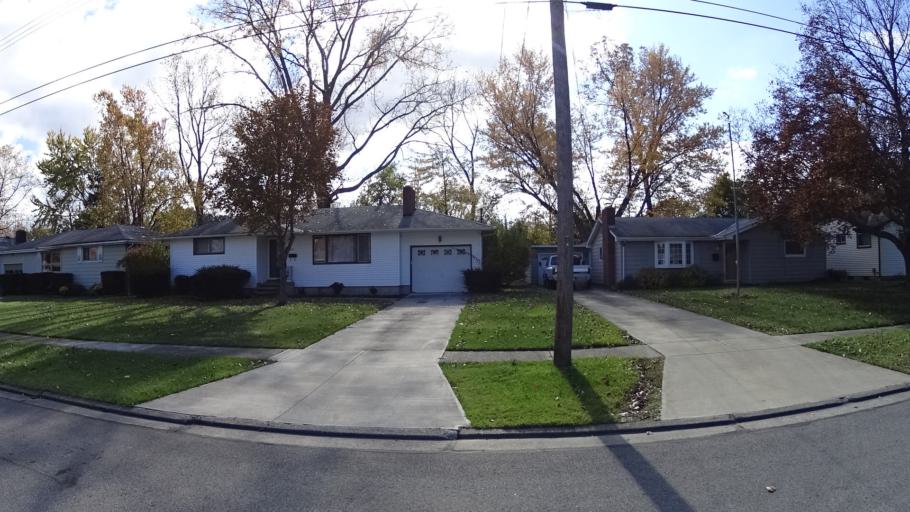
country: US
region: Ohio
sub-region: Lorain County
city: Lorain
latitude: 41.4469
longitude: -82.2179
